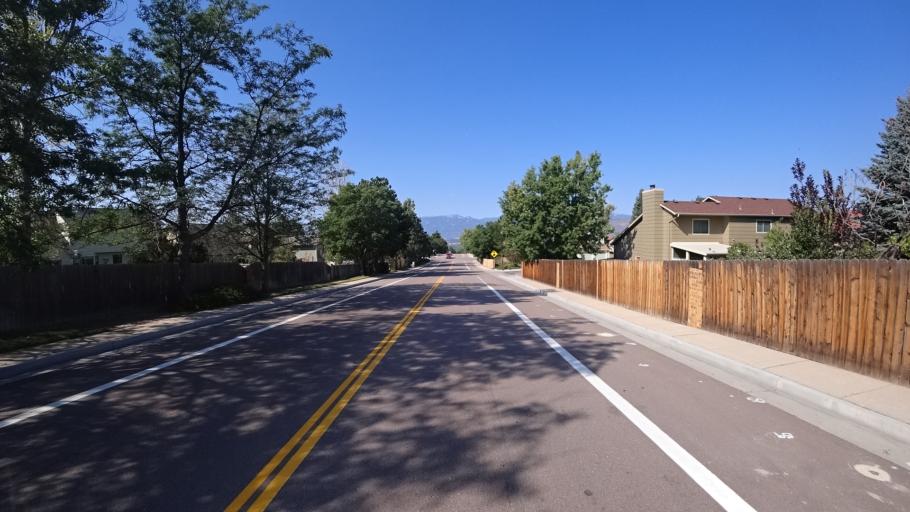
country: US
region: Colorado
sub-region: El Paso County
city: Air Force Academy
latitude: 38.9568
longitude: -104.7804
